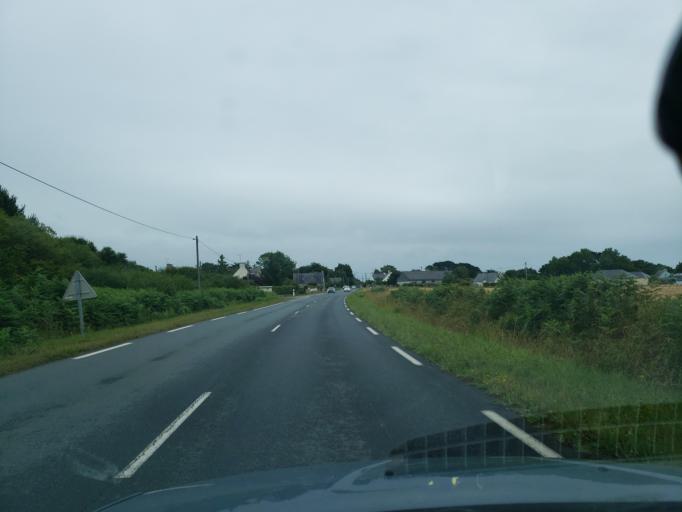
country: FR
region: Brittany
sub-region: Departement du Finistere
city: Plomeur
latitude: 47.8186
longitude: -4.3042
